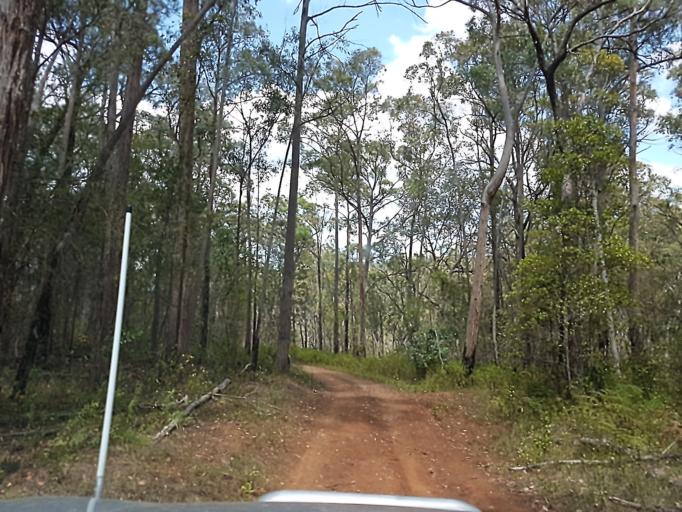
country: AU
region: Victoria
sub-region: East Gippsland
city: Lakes Entrance
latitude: -37.3487
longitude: 148.3576
